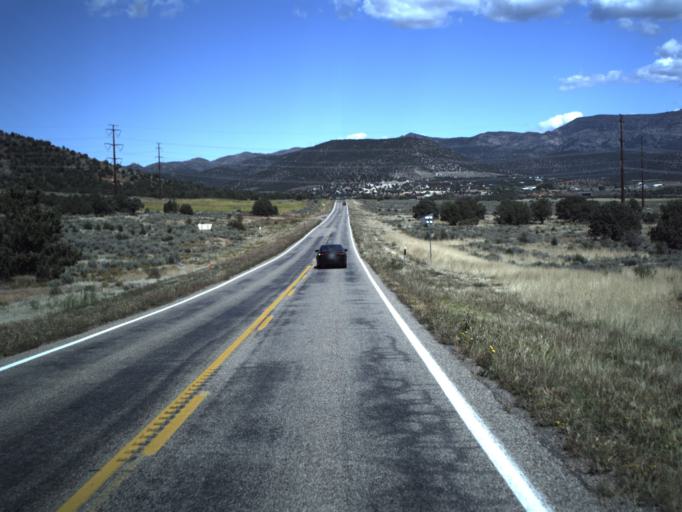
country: US
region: Utah
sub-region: Washington County
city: Enterprise
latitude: 37.3999
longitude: -113.6410
